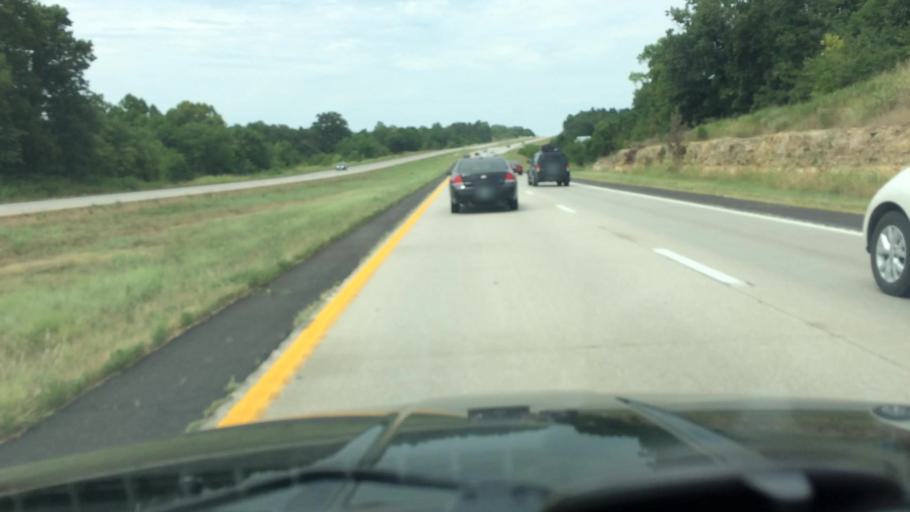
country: US
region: Missouri
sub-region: Greene County
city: Willard
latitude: 37.4319
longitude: -93.3552
